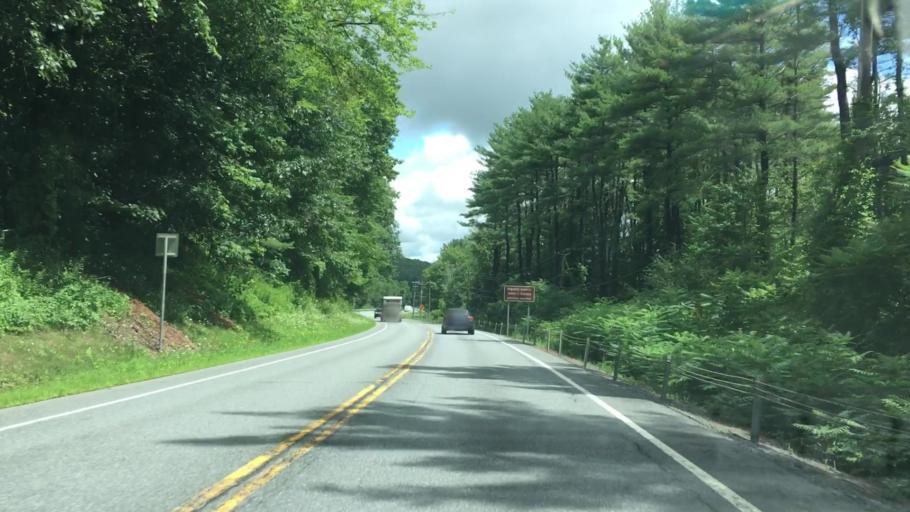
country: US
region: New York
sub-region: Rensselaer County
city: Poestenkill
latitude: 42.8177
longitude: -73.5269
